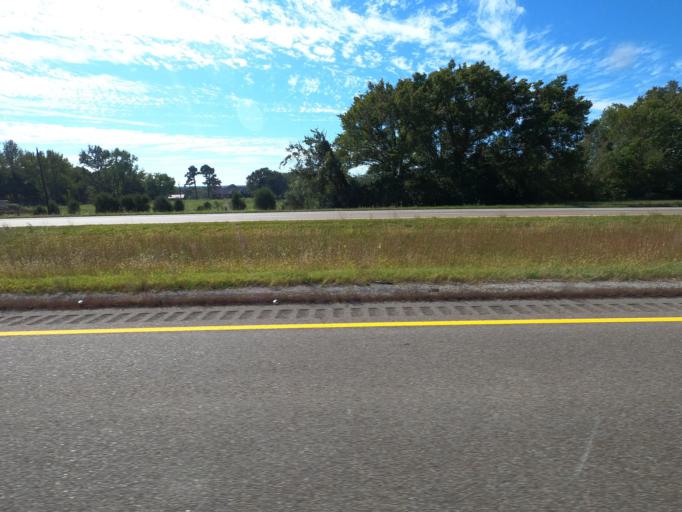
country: US
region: Tennessee
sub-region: Crockett County
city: Bells
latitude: 35.6779
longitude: -88.9693
